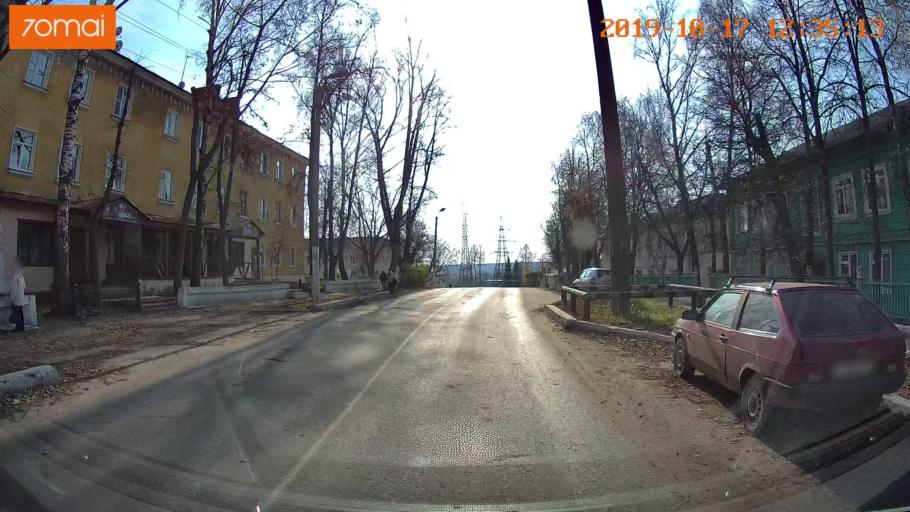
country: RU
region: Rjazan
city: Kasimov
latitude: 54.9449
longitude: 41.3702
